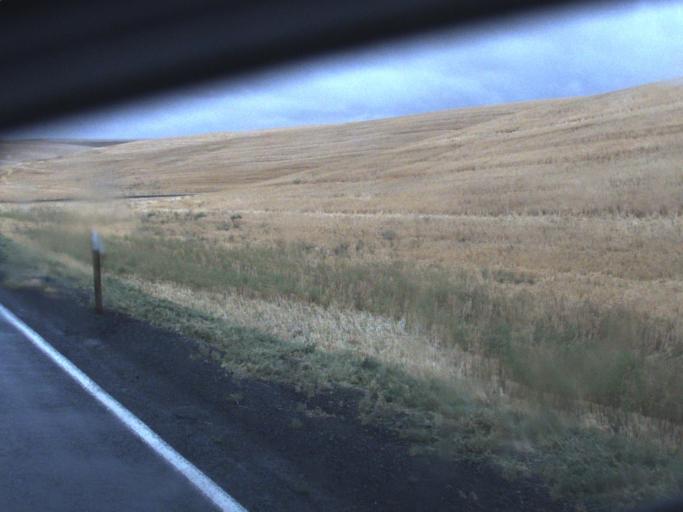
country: US
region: Washington
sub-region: Spokane County
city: Cheney
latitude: 47.1555
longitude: -117.8563
